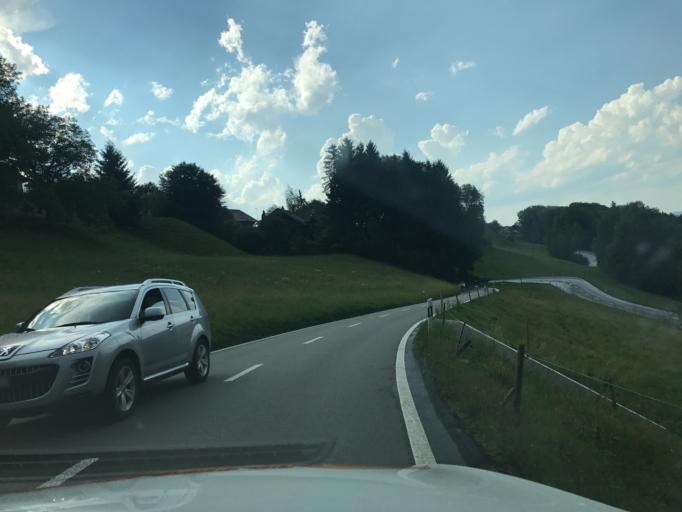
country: CH
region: Bern
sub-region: Thun District
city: Thierachern
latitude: 46.7316
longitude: 7.5863
